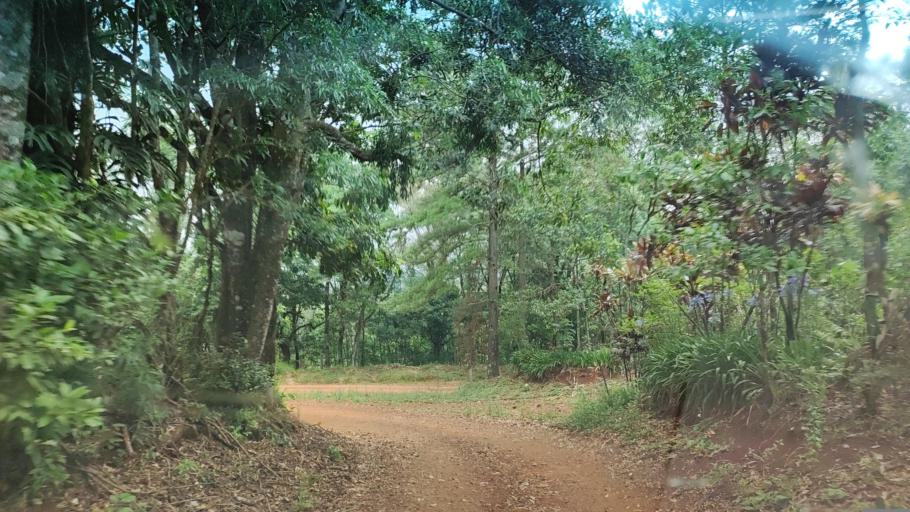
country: AR
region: Misiones
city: Dos de Mayo
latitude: -27.0074
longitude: -54.6227
